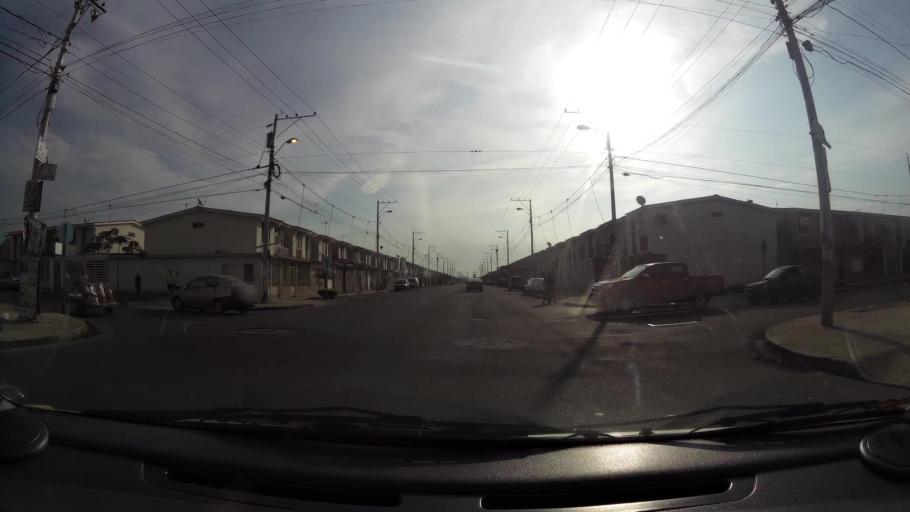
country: EC
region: Guayas
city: Eloy Alfaro
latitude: -2.0663
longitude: -79.8965
